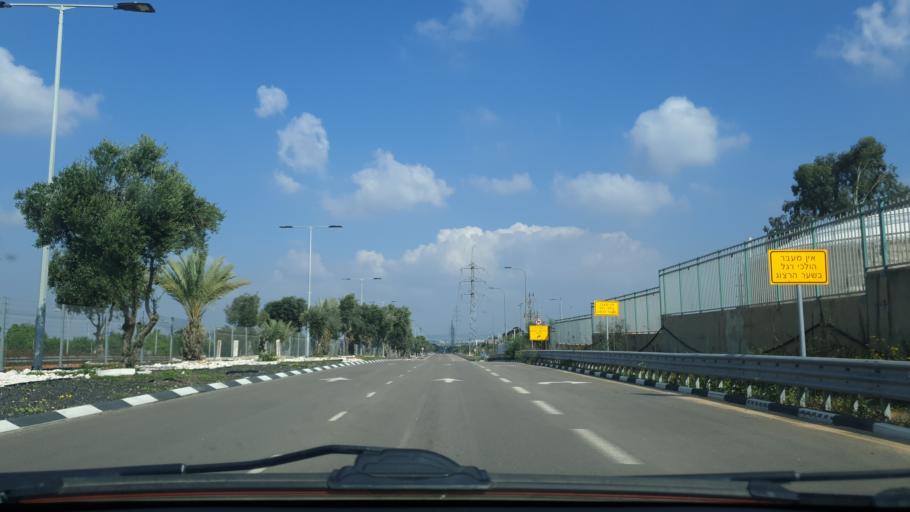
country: IL
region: Central District
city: Bet Dagan
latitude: 31.9688
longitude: 34.8292
